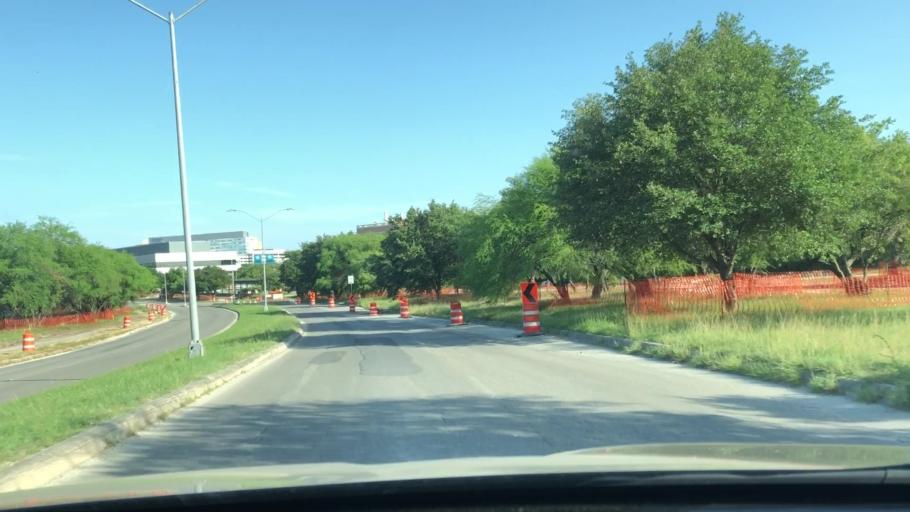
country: US
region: Texas
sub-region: Bexar County
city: Leon Valley
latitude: 29.5173
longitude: -98.5860
